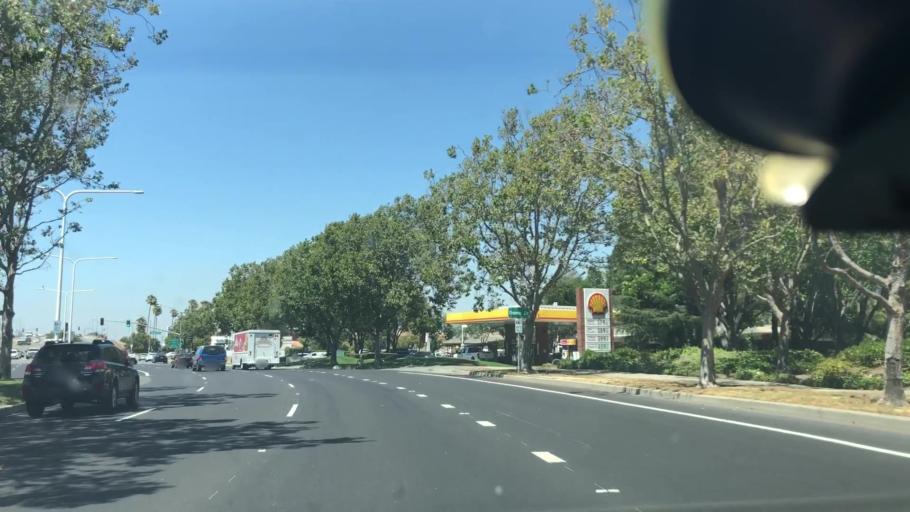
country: US
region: California
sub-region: Alameda County
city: Dublin
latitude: 37.6976
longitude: -121.9036
